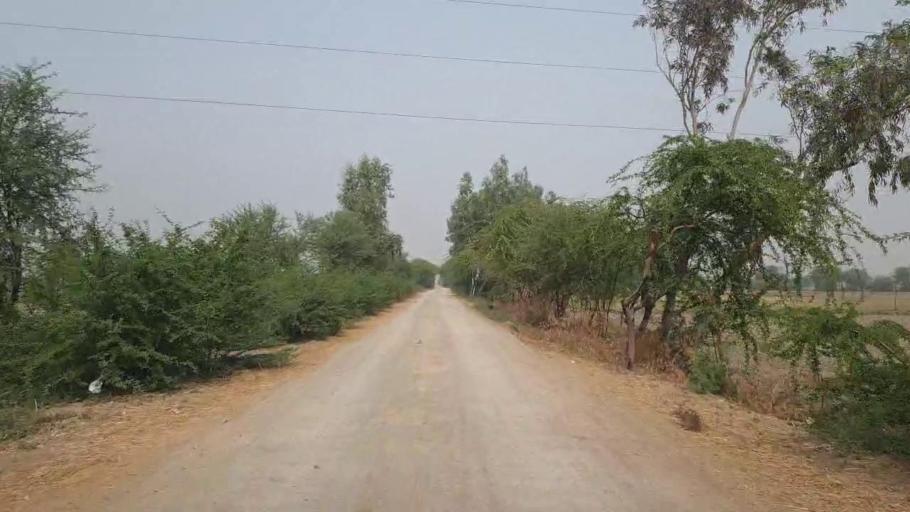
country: PK
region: Sindh
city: Kario
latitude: 24.6541
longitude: 68.6398
